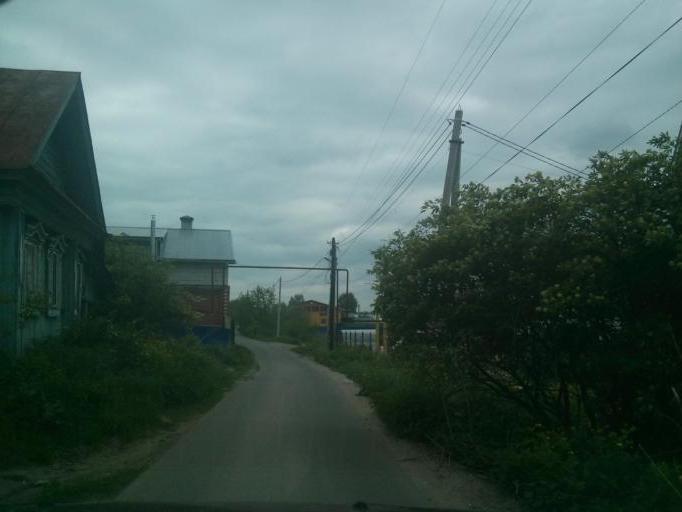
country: RU
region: Nizjnij Novgorod
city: Afonino
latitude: 56.2986
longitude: 44.1000
